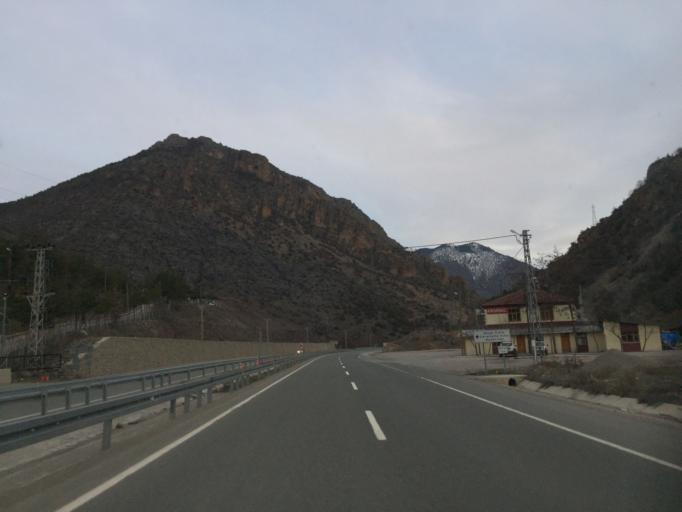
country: TR
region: Gumushane
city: Gumushkhane
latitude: 40.5245
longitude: 39.3951
